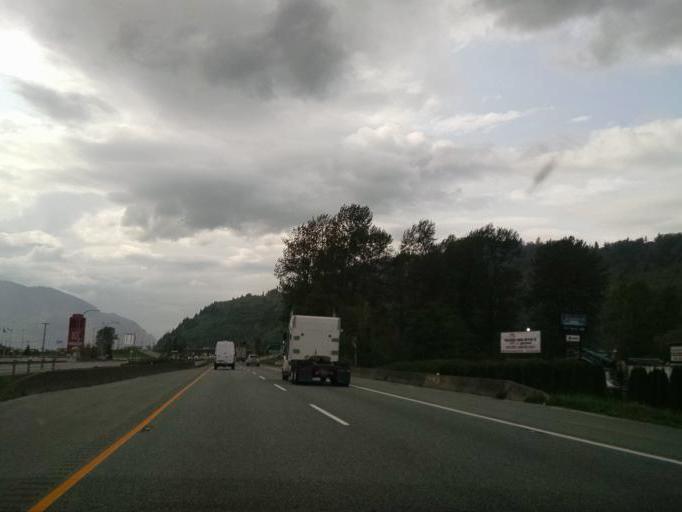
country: CA
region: British Columbia
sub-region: Fraser Valley Regional District
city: Chilliwack
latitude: 49.1442
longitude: -121.9983
